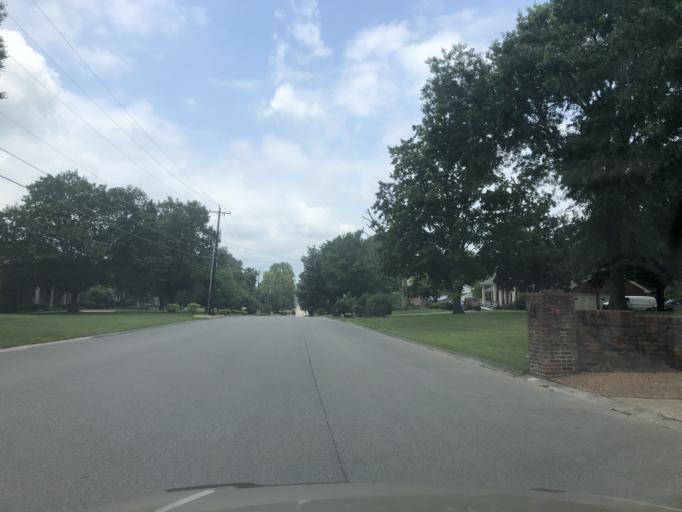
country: US
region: Tennessee
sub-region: Davidson County
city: Lakewood
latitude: 36.2336
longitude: -86.6183
